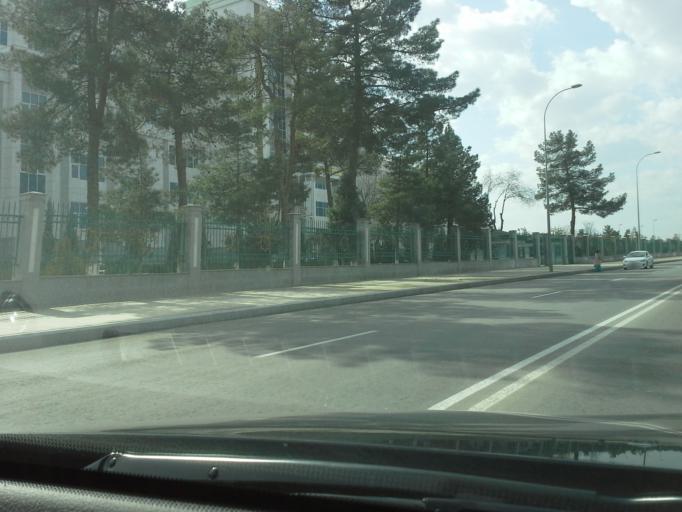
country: TM
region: Ahal
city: Ashgabat
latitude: 37.9530
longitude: 58.3335
